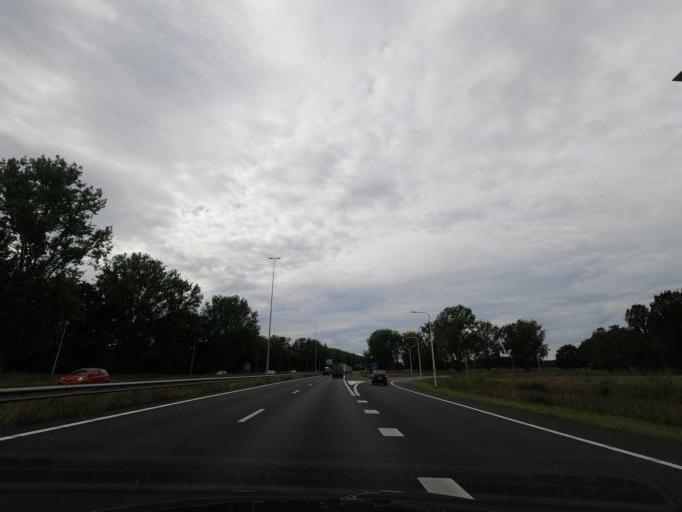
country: NL
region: Gelderland
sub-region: Gemeente Maasdriel
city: Hedel
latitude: 51.6967
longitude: 5.2441
